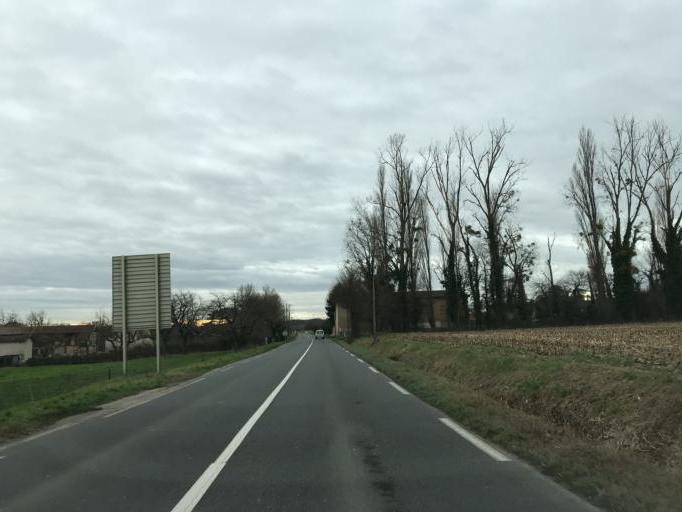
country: FR
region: Rhone-Alpes
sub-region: Departement de l'Ain
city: Sainte-Euphemie
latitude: 45.9806
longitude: 4.7977
